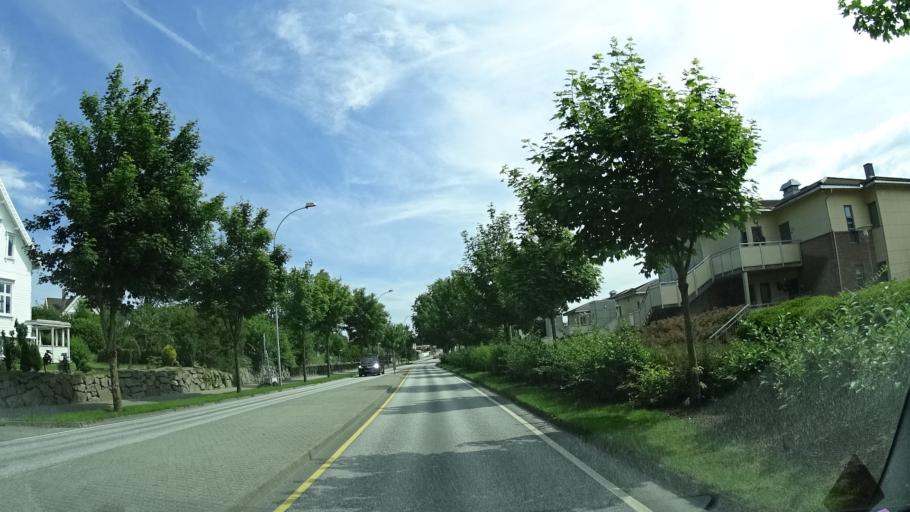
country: NO
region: Rogaland
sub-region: Stavanger
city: Stavanger
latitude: 58.9789
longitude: 5.6946
